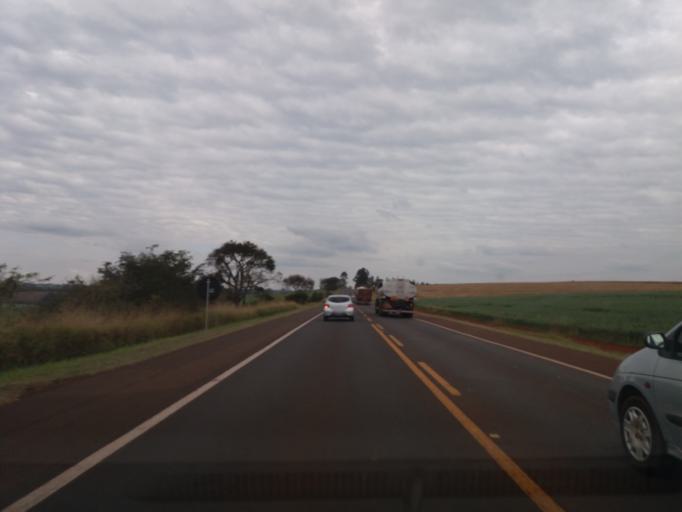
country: BR
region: Parana
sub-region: Corbelia
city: Corbelia
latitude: -24.8831
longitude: -53.3458
